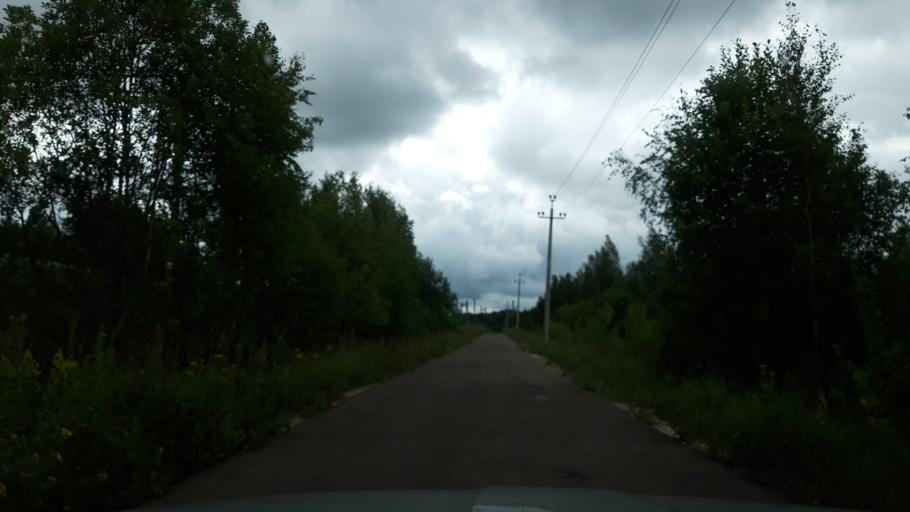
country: RU
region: Moskovskaya
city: Povarovo
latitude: 56.0411
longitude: 37.0541
